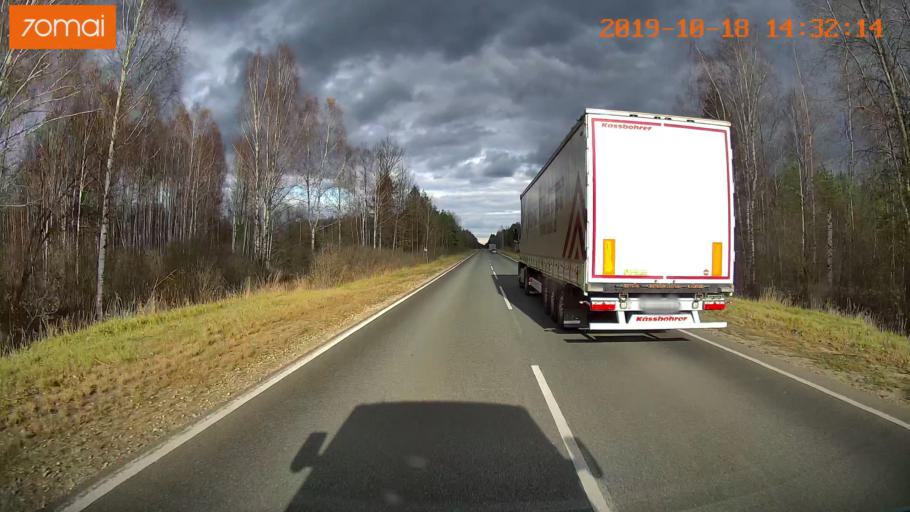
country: RU
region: Rjazan
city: Tuma
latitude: 55.1894
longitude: 40.5766
